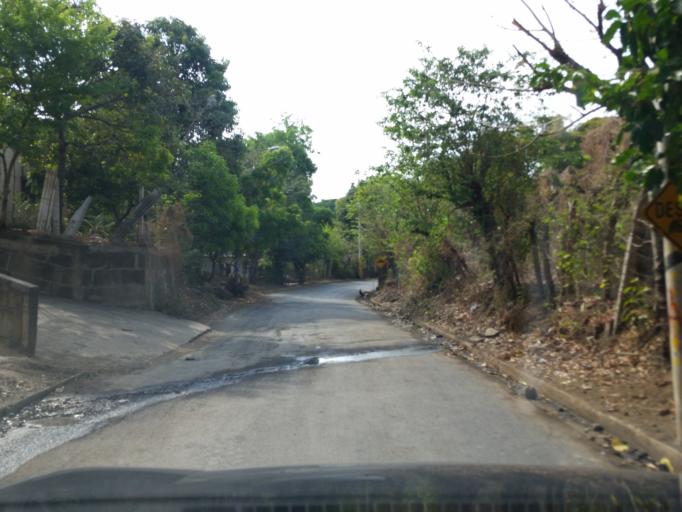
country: NI
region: Managua
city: Managua
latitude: 12.0837
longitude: -86.2192
